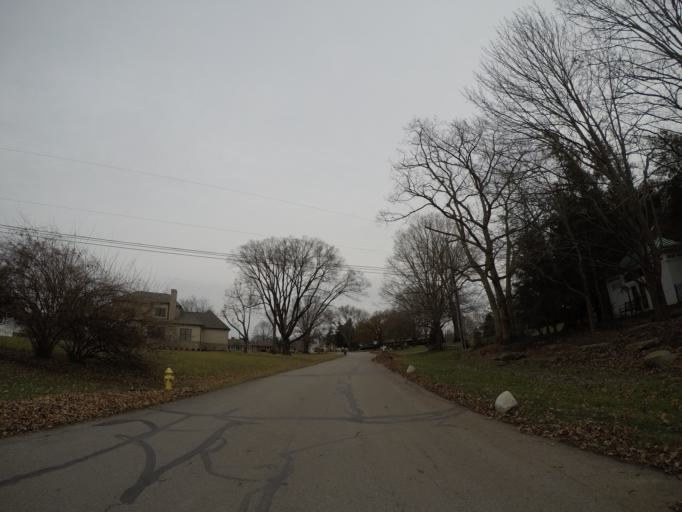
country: US
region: Ohio
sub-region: Franklin County
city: Dublin
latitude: 40.0580
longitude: -83.0944
